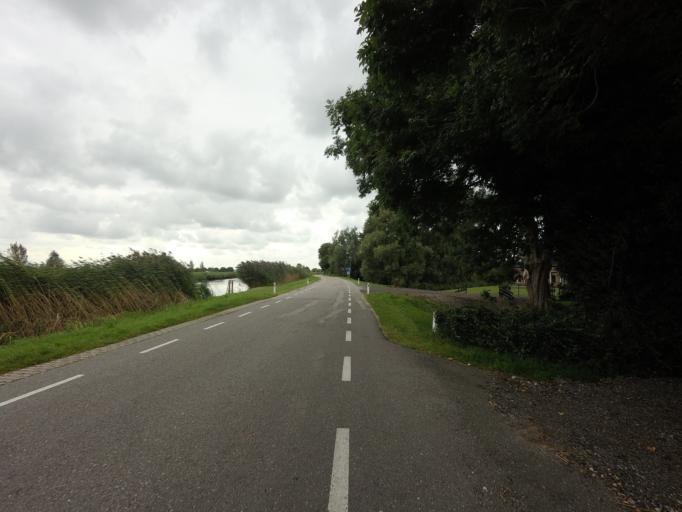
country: NL
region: North Holland
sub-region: Gemeente Purmerend
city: Purmerend
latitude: 52.5247
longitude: 4.9992
